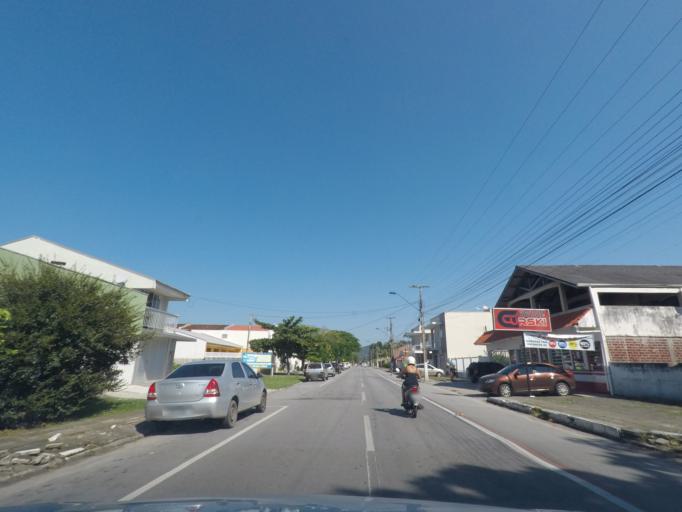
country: BR
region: Parana
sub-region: Guaratuba
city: Guaratuba
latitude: -25.8213
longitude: -48.5348
